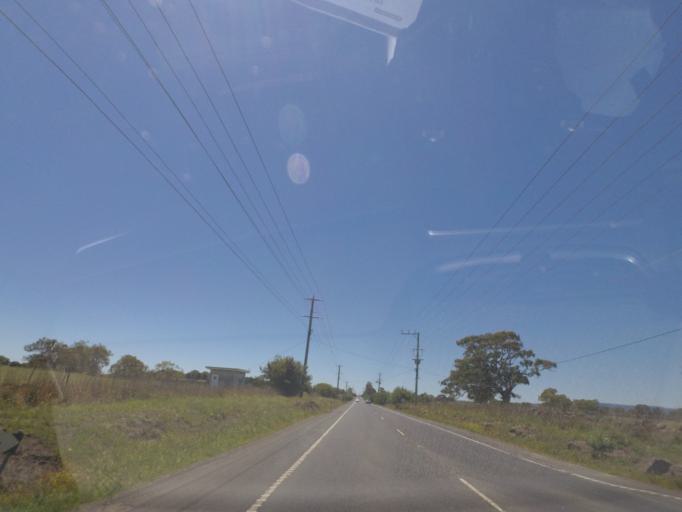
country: AU
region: Victoria
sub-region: Whittlesea
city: Mernda
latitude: -37.5812
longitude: 145.0331
